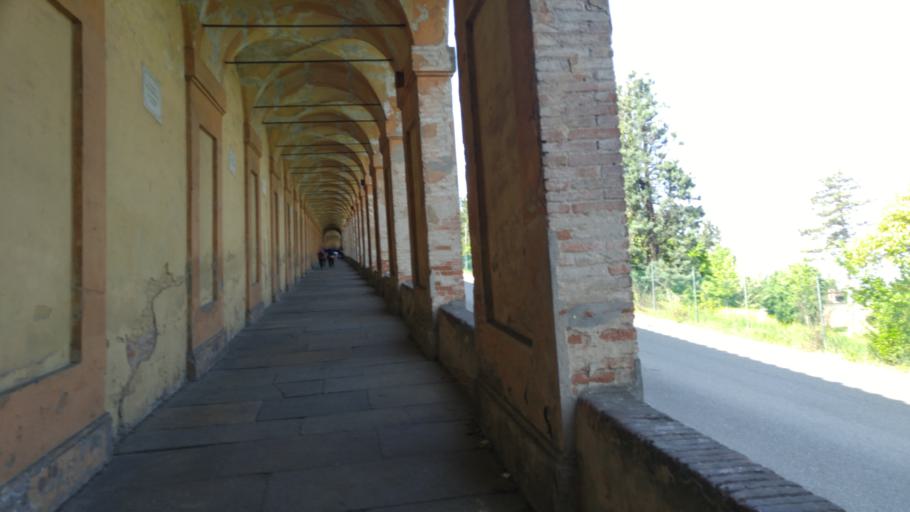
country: IT
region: Emilia-Romagna
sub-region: Provincia di Bologna
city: Bologna
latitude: 44.4887
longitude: 11.3086
